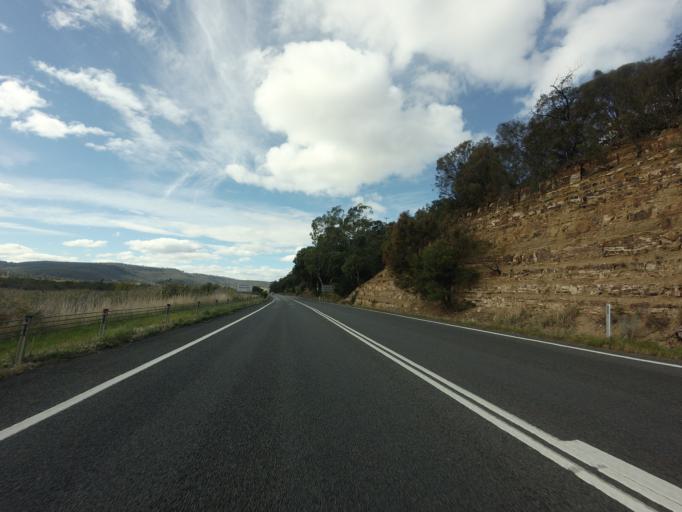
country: AU
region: Tasmania
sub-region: Glenorchy
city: Granton
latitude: -42.7502
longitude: 147.1742
